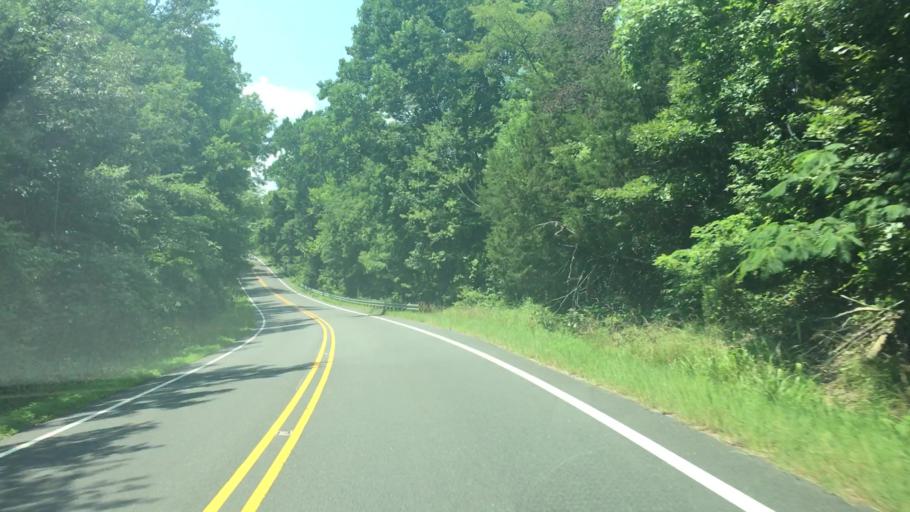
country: US
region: Virginia
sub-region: King George County
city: Passapatanzy
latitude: 38.2972
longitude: -77.3093
